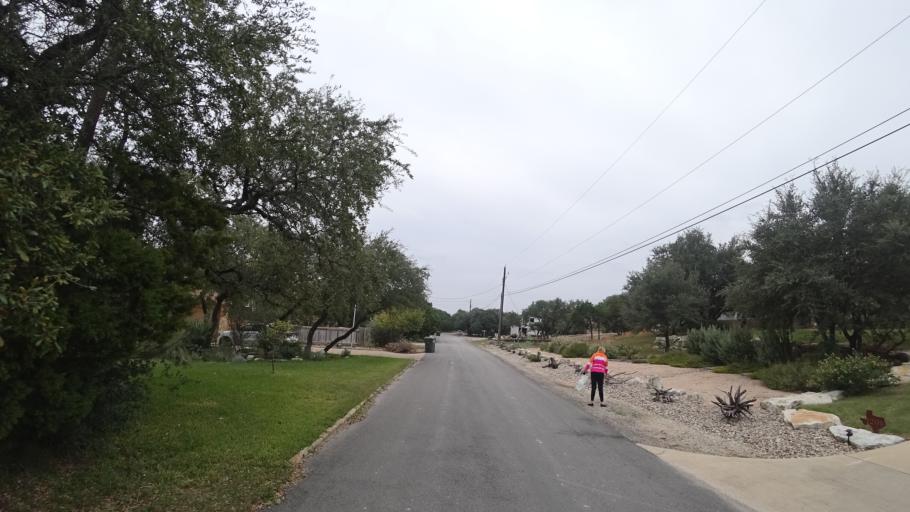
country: US
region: Texas
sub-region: Travis County
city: Hudson Bend
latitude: 30.3690
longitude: -97.9310
